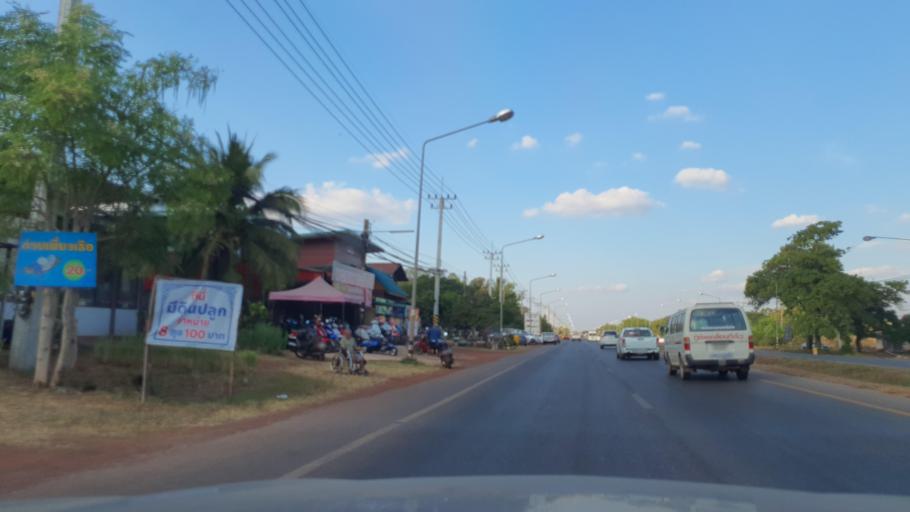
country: TH
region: Sakon Nakhon
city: Sakon Nakhon
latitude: 17.2294
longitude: 104.1071
